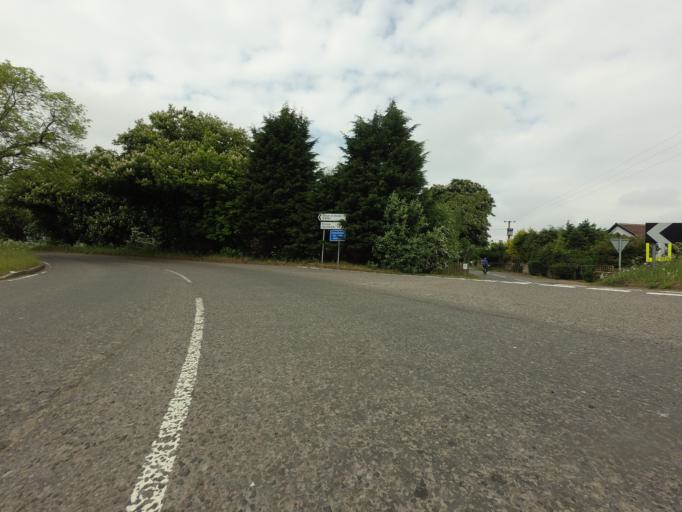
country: GB
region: Scotland
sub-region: Perth and Kinross
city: Kinross
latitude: 56.1684
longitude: -3.4470
